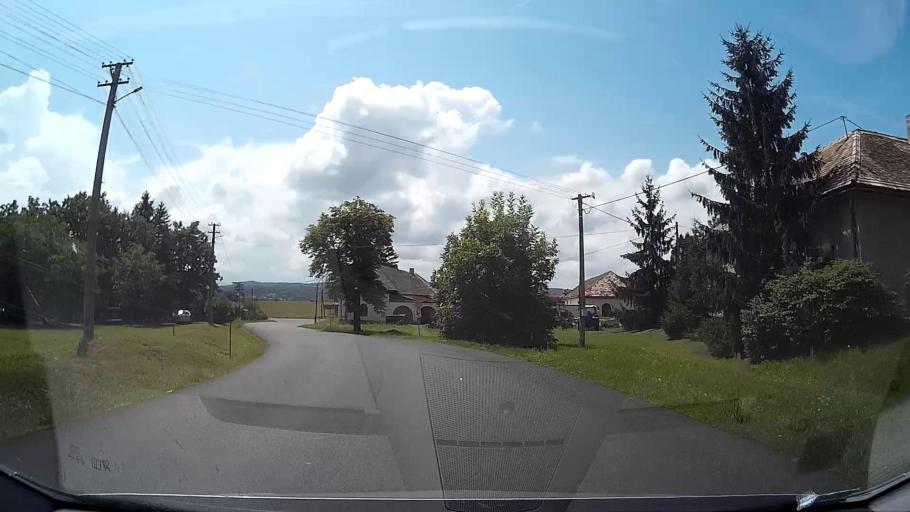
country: SK
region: Banskobystricky
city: Fil'akovo
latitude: 48.3071
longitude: 19.8001
